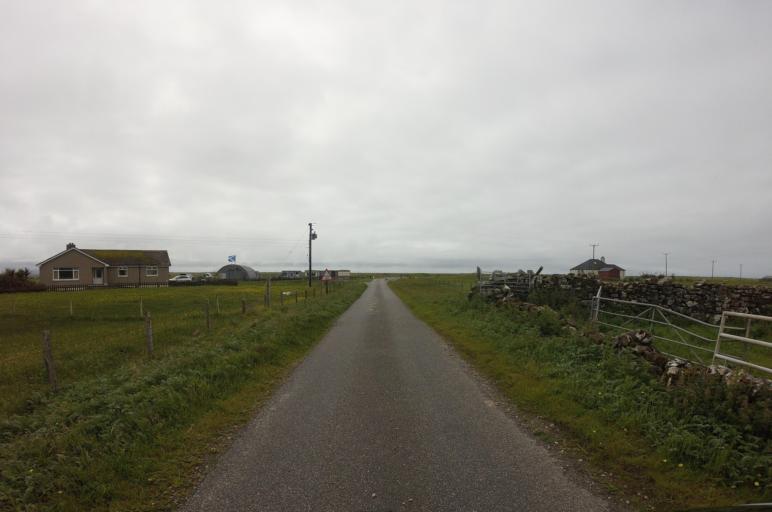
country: GB
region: Scotland
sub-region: Eilean Siar
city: Isle of North Uist
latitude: 57.5285
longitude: -7.3613
